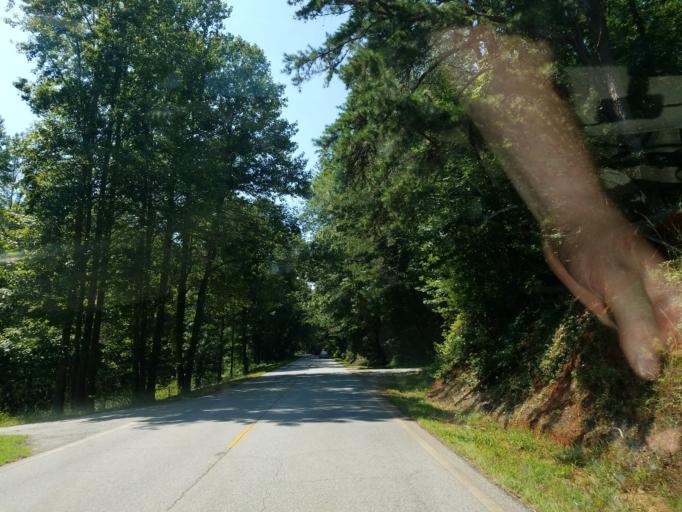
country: US
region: Georgia
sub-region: Lumpkin County
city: Dahlonega
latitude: 34.6343
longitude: -83.9287
